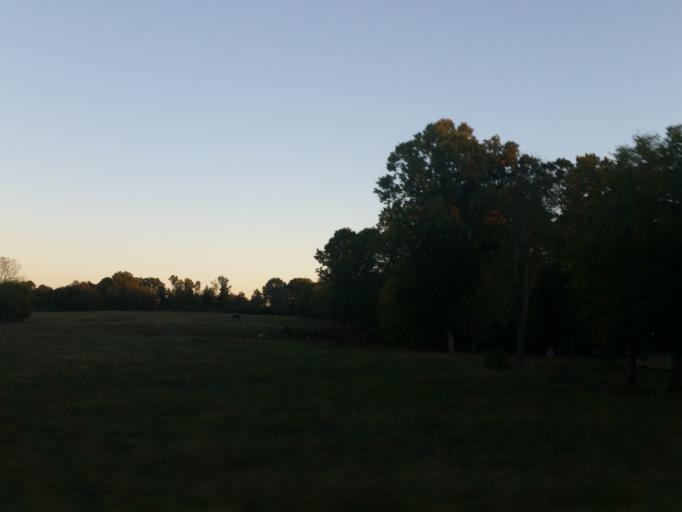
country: US
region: Tennessee
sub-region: Union County
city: Condon
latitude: 36.1353
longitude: -83.8109
